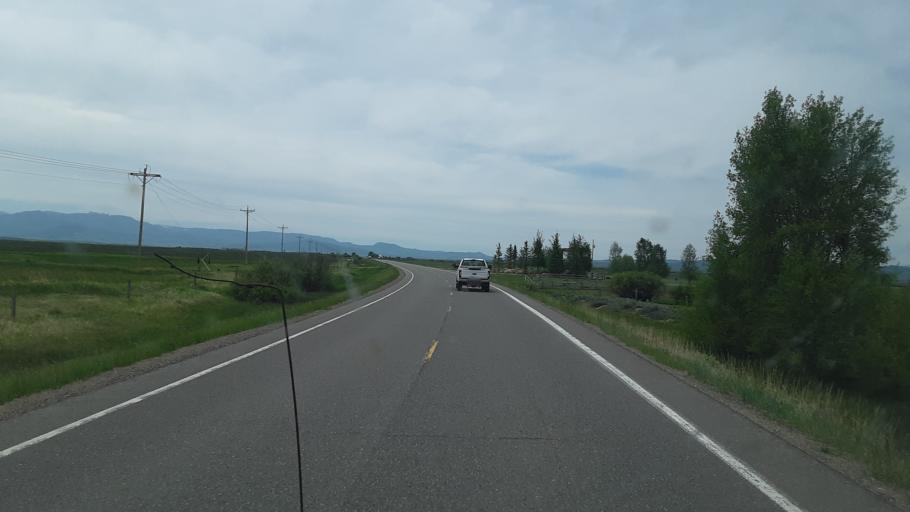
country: US
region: Colorado
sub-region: Jackson County
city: Walden
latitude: 40.6114
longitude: -106.4066
